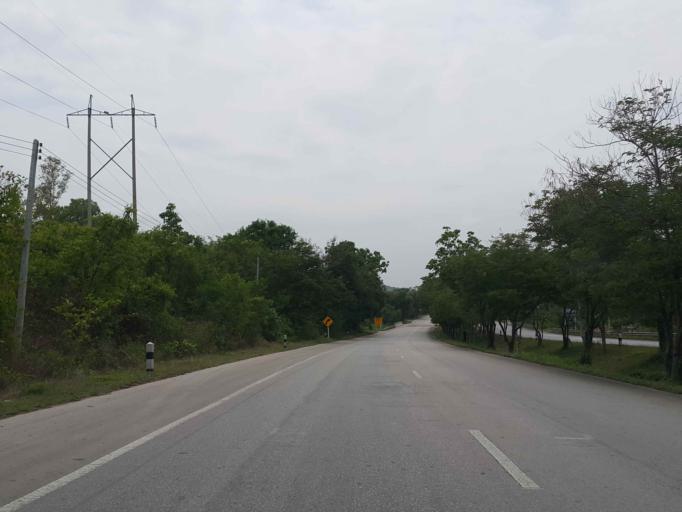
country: TH
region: Lampang
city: Sop Prap
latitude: 17.8643
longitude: 99.3323
